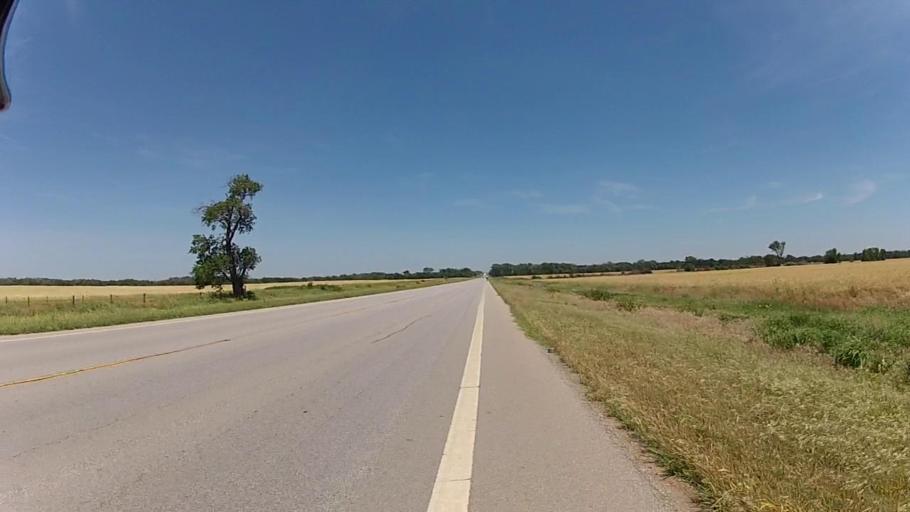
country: US
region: Kansas
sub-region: Harper County
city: Harper
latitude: 37.2392
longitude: -98.1049
